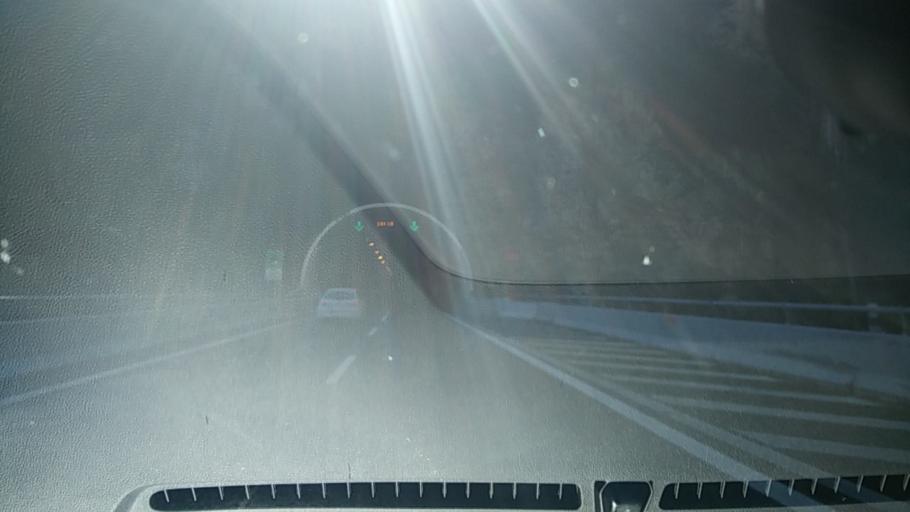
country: IT
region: Friuli Venezia Giulia
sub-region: Provincia di Udine
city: Moggio di Sotto
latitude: 46.3967
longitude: 13.1802
